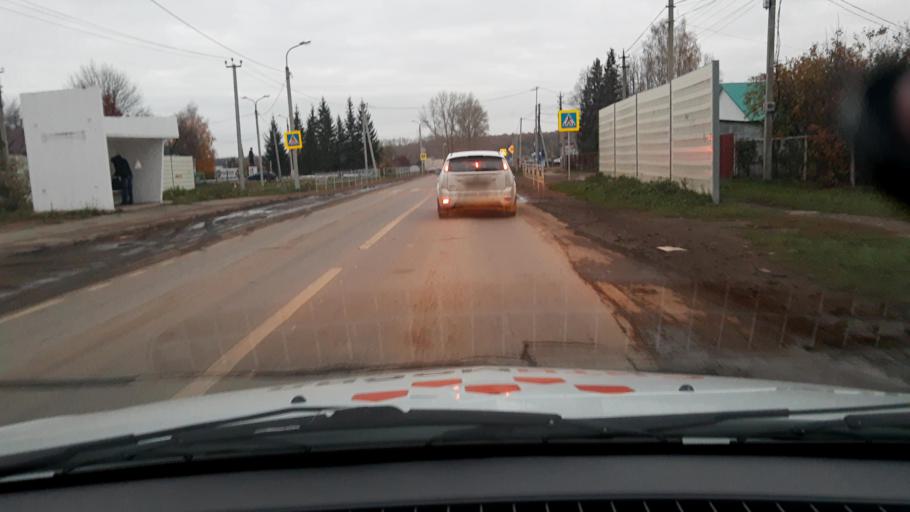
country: RU
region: Bashkortostan
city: Kabakovo
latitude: 54.6884
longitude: 56.1340
